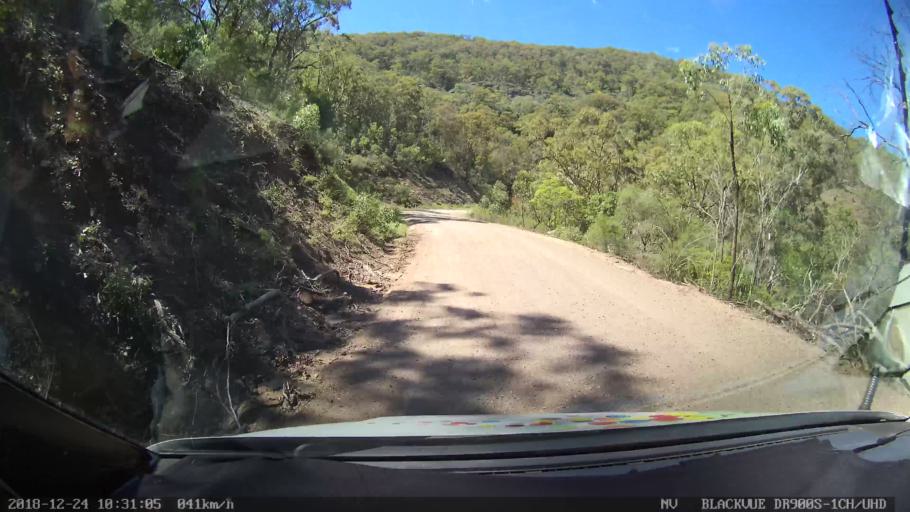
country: AU
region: New South Wales
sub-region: Upper Hunter Shire
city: Merriwa
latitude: -31.8380
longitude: 150.5230
